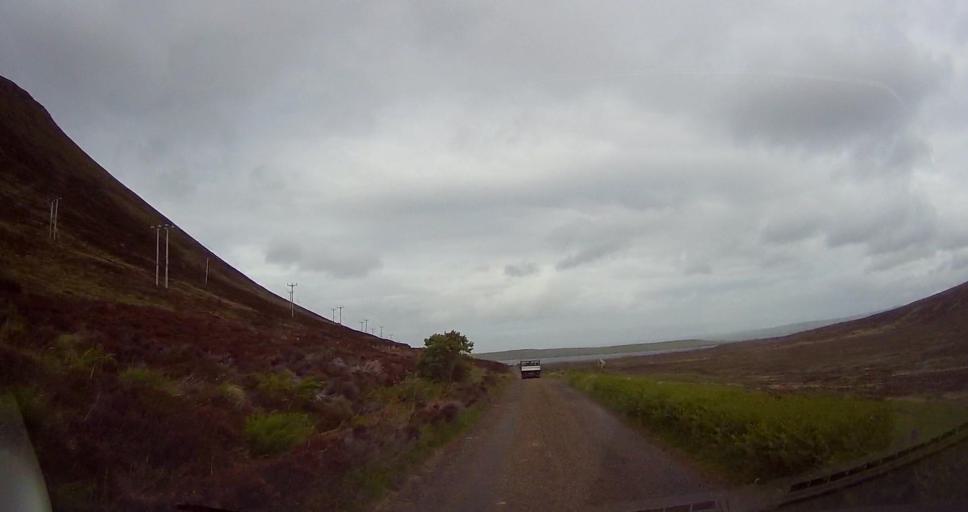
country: GB
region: Scotland
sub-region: Orkney Islands
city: Stromness
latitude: 58.8895
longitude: -3.3155
